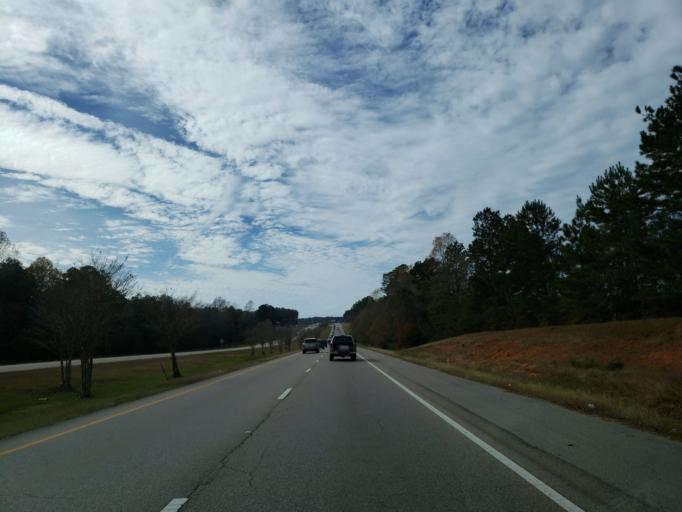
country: US
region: Mississippi
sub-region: Lamar County
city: West Hattiesburg
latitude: 31.3142
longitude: -89.4589
